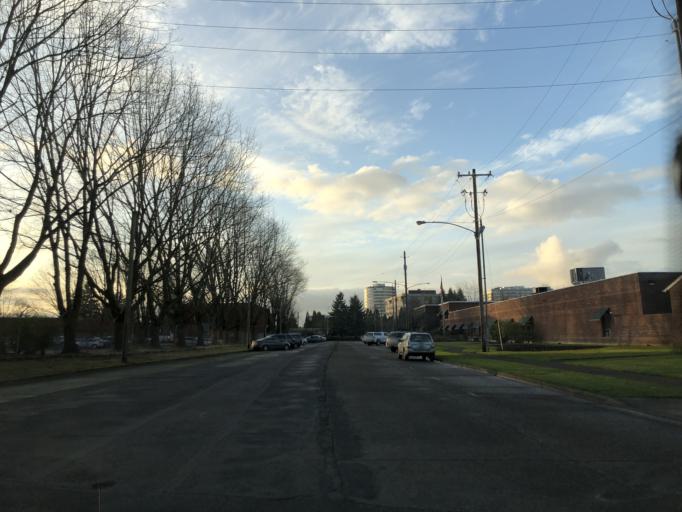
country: US
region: Washington
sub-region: Clark County
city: Vancouver
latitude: 45.6246
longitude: -122.6659
